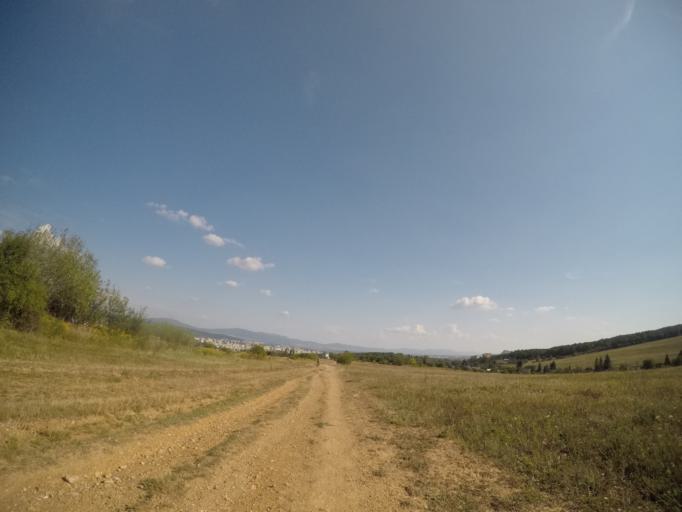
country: SK
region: Kosicky
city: Kosice
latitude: 48.7298
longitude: 21.2163
